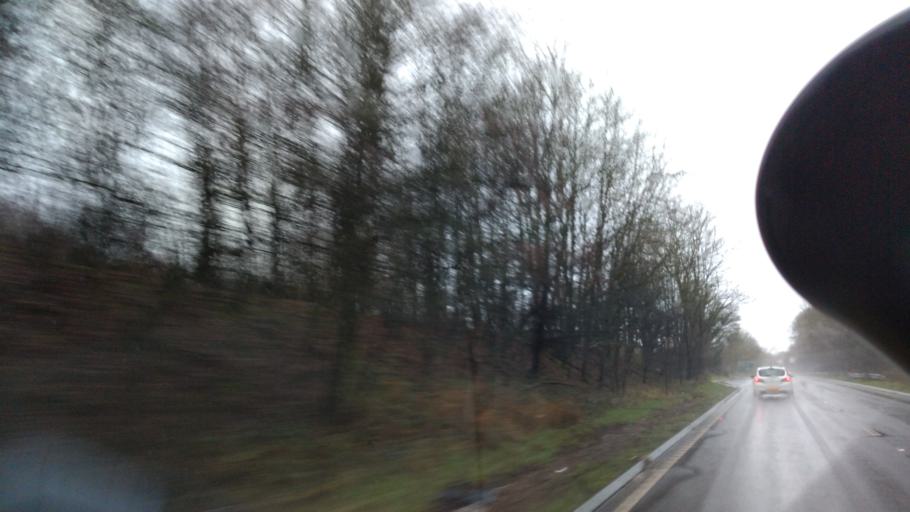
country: GB
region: England
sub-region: Brighton and Hove
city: Rottingdean
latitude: 50.8656
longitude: -0.0635
